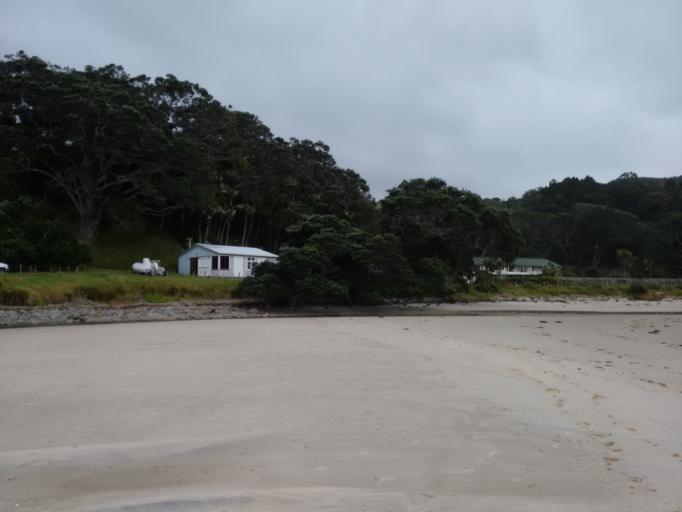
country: NZ
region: Waikato
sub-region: Thames-Coromandel District
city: Coromandel
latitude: -36.7072
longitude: 175.6086
